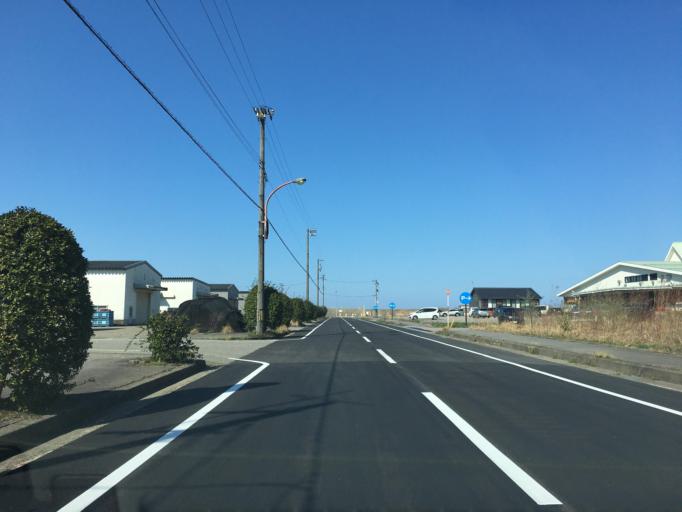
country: JP
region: Toyama
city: Nishishinminato
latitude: 36.7806
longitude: 137.0985
